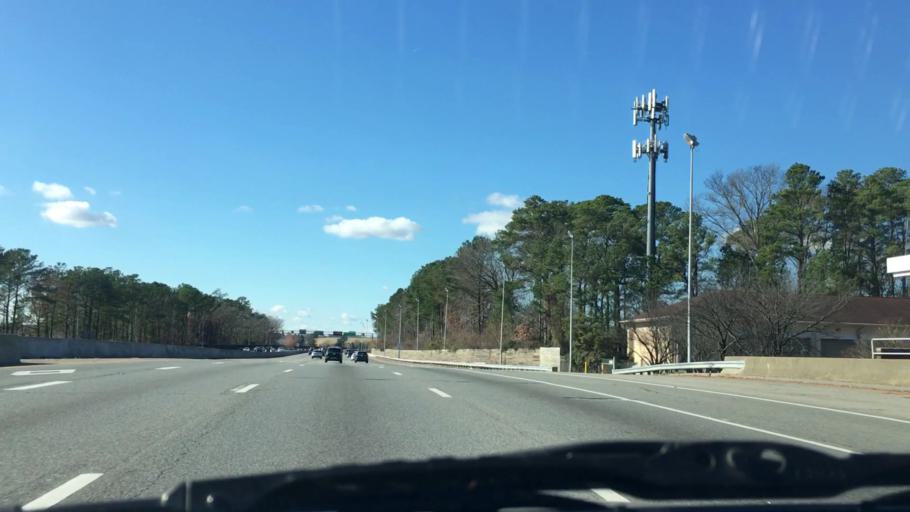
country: US
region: Virginia
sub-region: City of Virginia Beach
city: Virginia Beach
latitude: 36.8343
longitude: -76.1109
